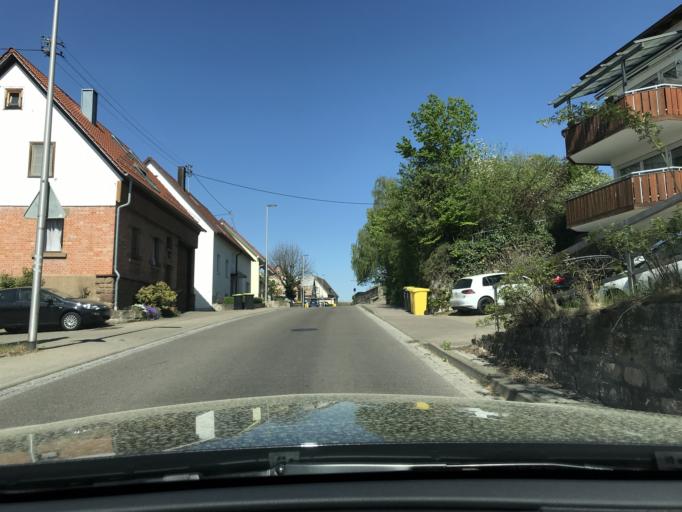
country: DE
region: Baden-Wuerttemberg
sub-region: Regierungsbezirk Stuttgart
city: Korb
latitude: 48.8307
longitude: 9.3731
